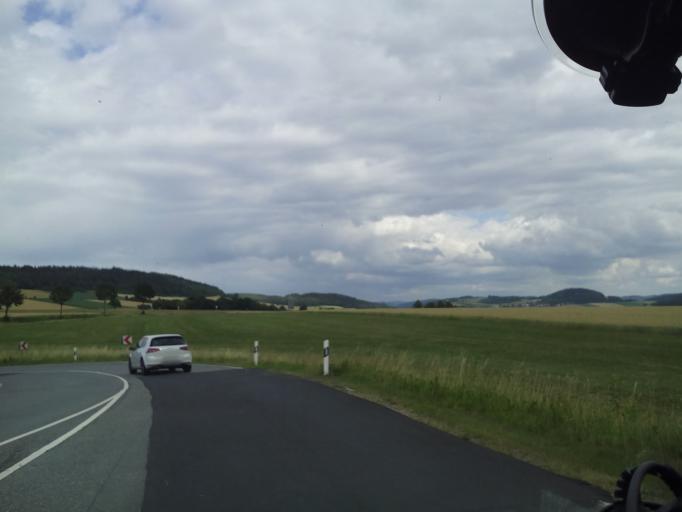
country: DE
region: Bavaria
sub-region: Upper Franconia
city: Rodental
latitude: 50.2737
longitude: 11.0958
